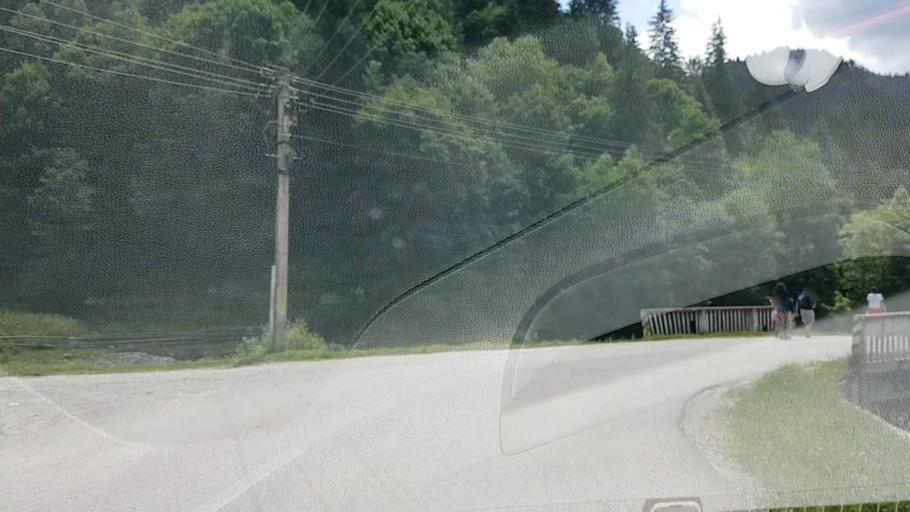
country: RO
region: Suceava
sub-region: Comuna Crucea
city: Crucea
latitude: 47.4157
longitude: 25.5852
